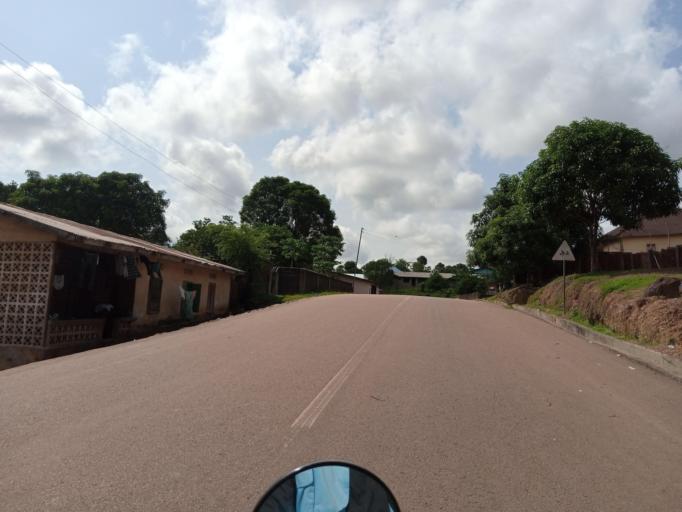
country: SL
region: Southern Province
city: Bo
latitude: 7.9706
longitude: -11.7364
